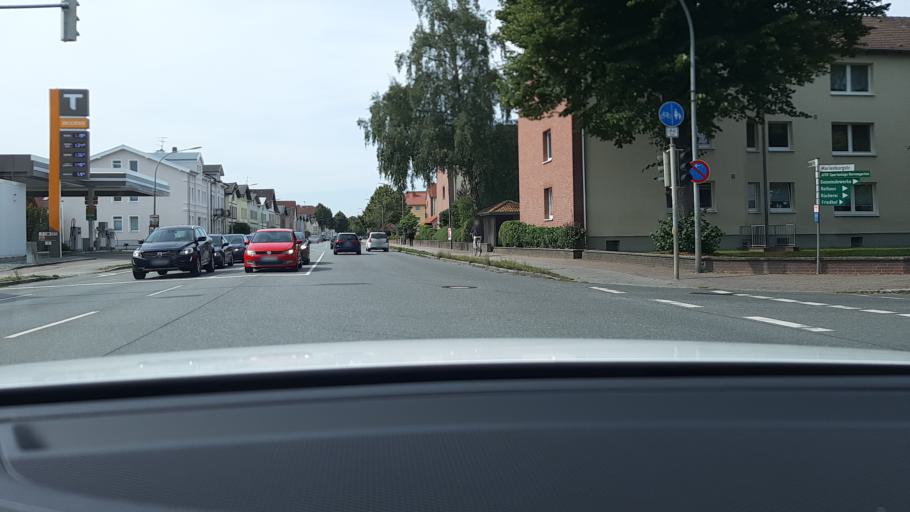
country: DE
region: Schleswig-Holstein
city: Stockelsdorf
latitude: 53.8878
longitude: 10.6459
